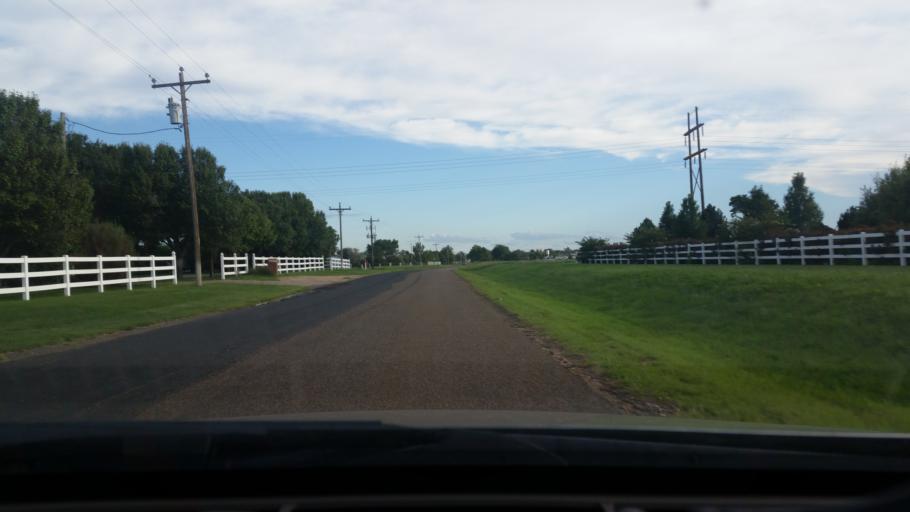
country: US
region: New Mexico
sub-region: Curry County
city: Clovis
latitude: 34.4565
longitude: -103.1785
